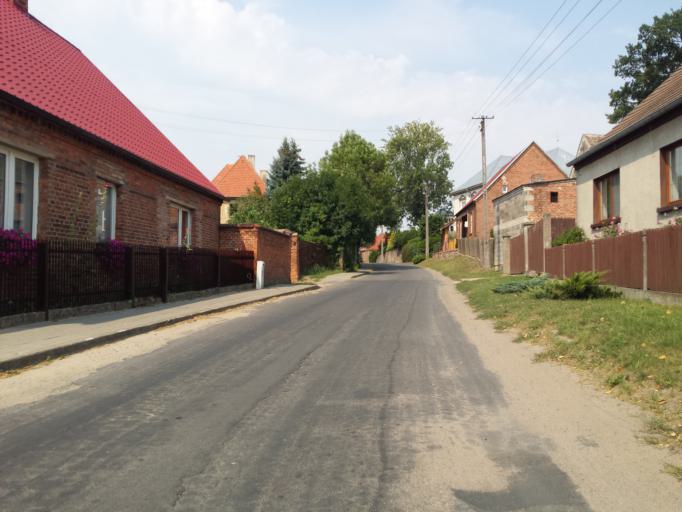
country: PL
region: Greater Poland Voivodeship
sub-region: Powiat czarnkowsko-trzcianecki
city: Polajewo
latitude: 52.7730
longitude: 16.6439
